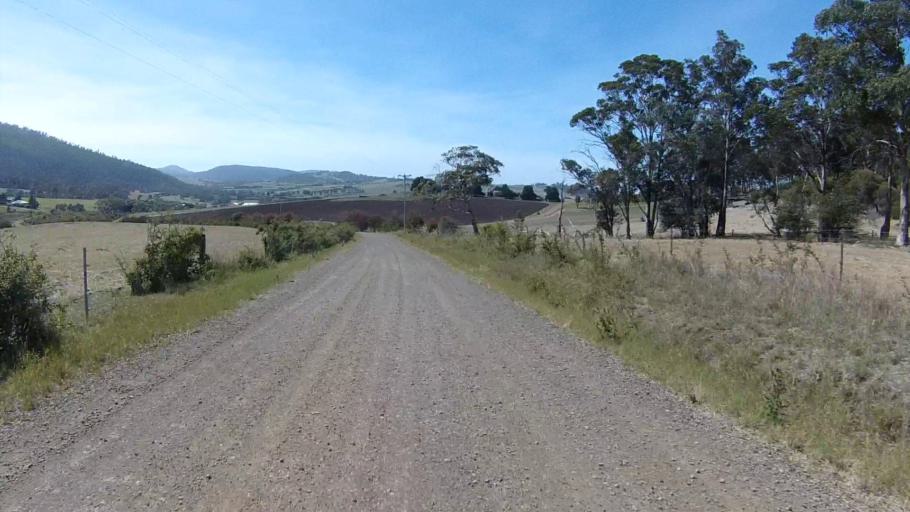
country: AU
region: Tasmania
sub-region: Sorell
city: Sorell
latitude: -42.7454
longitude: 147.6032
